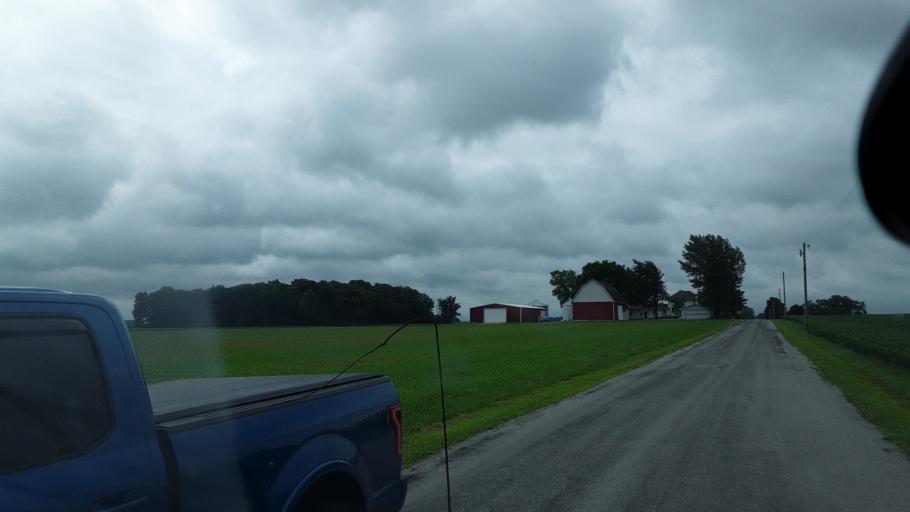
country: US
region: Indiana
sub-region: Wells County
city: Ossian
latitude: 40.8593
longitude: -85.1014
